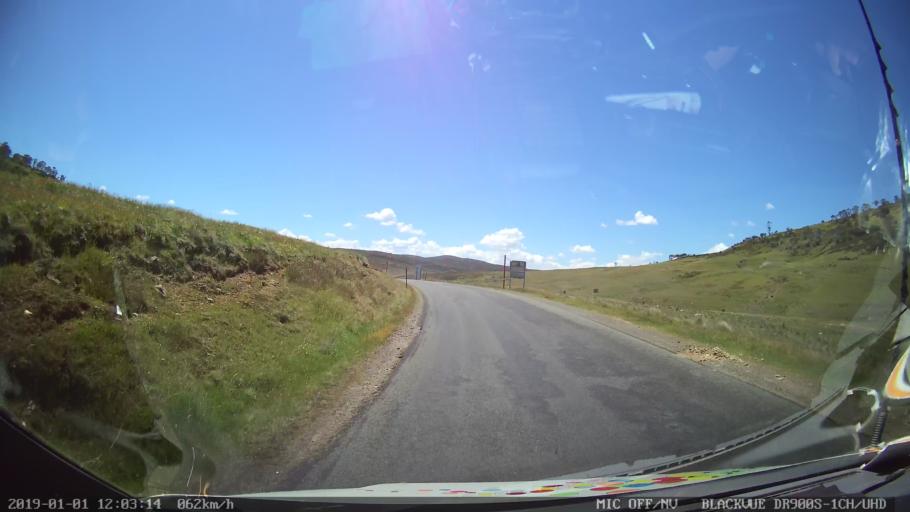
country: AU
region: New South Wales
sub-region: Snowy River
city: Jindabyne
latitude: -35.8697
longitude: 148.4845
